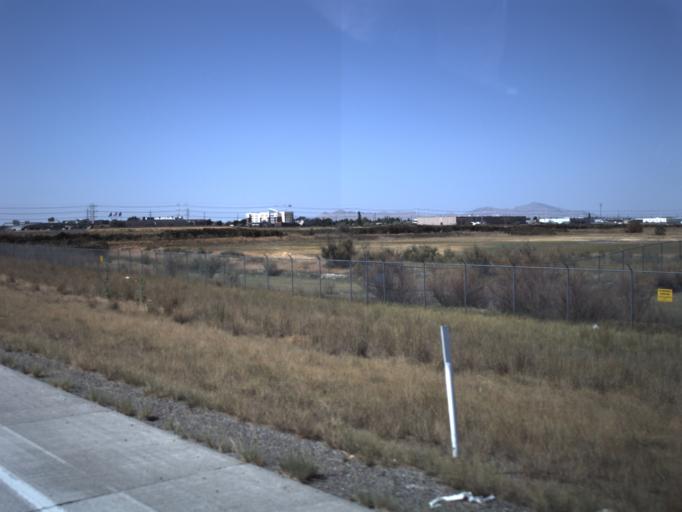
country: US
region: Utah
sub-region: Salt Lake County
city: West Valley City
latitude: 40.7660
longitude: -111.9915
